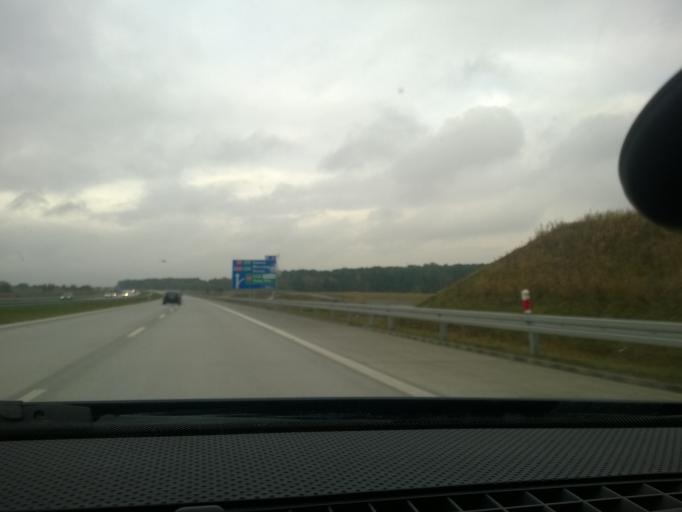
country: PL
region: Lodz Voivodeship
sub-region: Powiat lodzki wschodni
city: Andrespol
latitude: 51.7825
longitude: 19.6114
